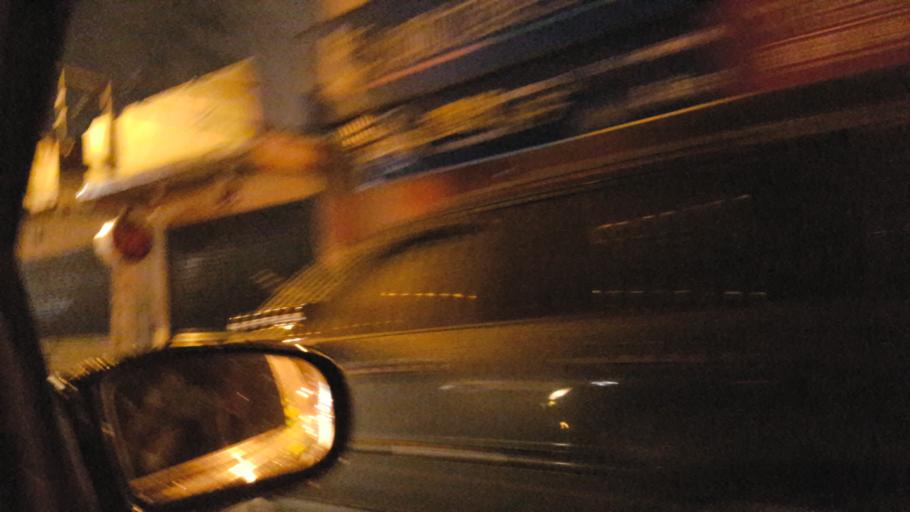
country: TW
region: Taiwan
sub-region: Hsinchu
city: Zhubei
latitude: 24.8294
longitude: 121.0070
